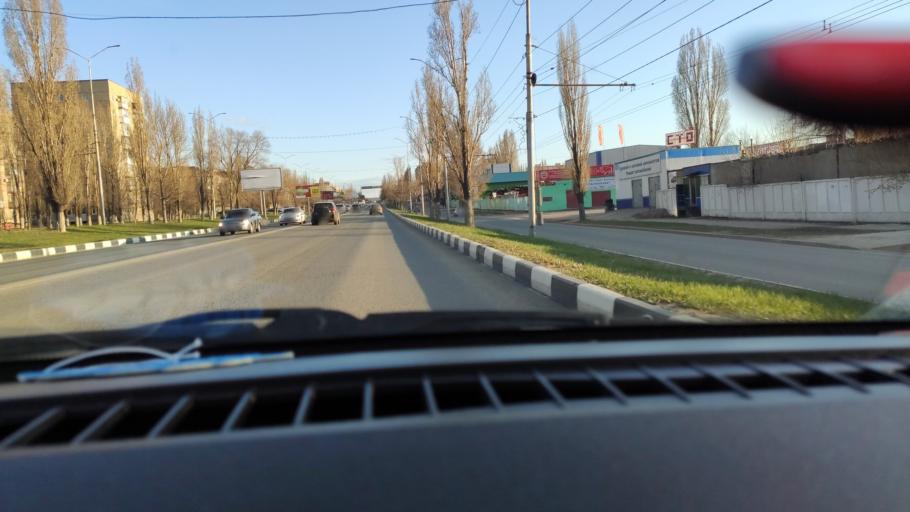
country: RU
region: Saratov
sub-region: Saratovskiy Rayon
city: Saratov
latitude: 51.6036
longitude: 45.9688
